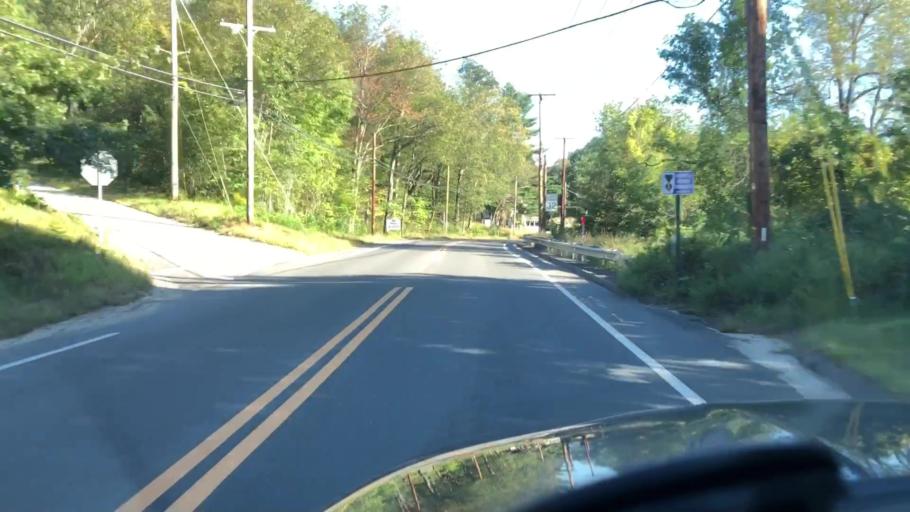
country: US
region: Massachusetts
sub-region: Hampden County
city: Palmer
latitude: 42.1418
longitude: -72.3117
